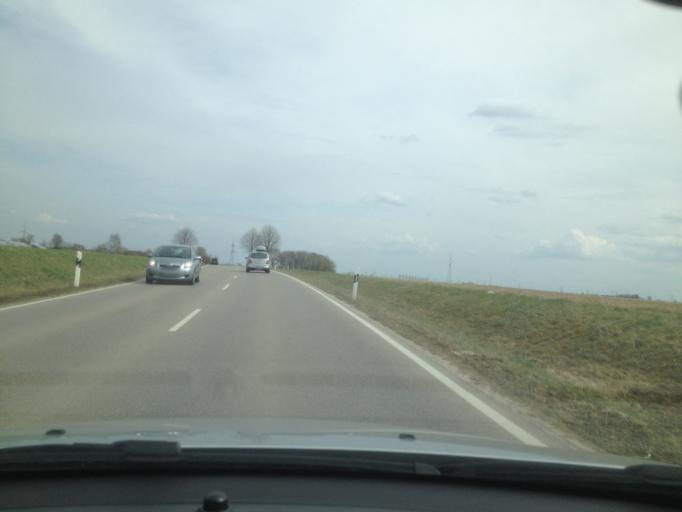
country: DE
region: Bavaria
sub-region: Swabia
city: Bobingen
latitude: 48.2545
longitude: 10.8313
